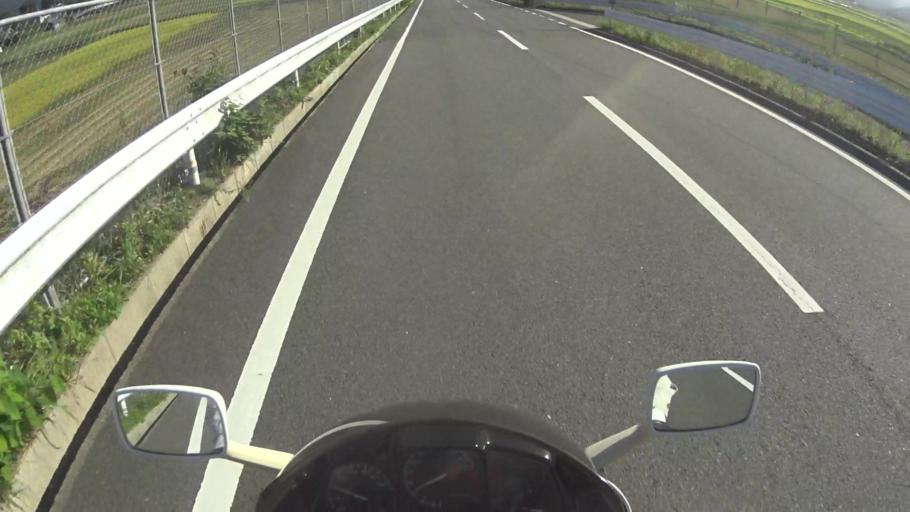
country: JP
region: Kyoto
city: Kameoka
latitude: 35.0944
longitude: 135.5514
